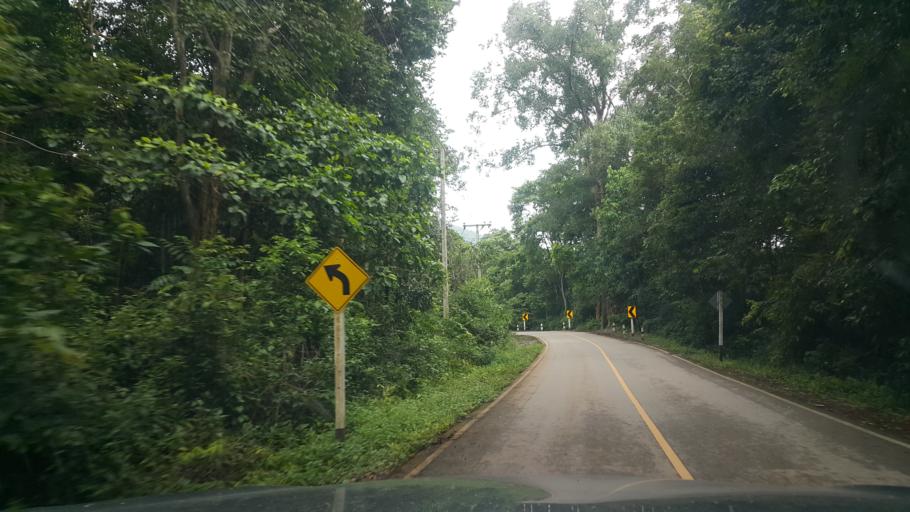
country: TH
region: Chiang Mai
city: San Sai
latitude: 18.9937
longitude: 99.1256
